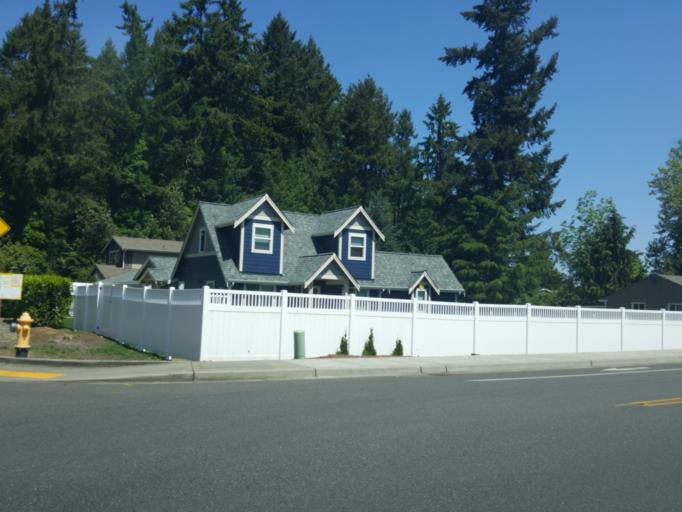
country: US
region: Washington
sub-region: Pierce County
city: Steilacoom
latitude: 47.1712
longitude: -122.5911
